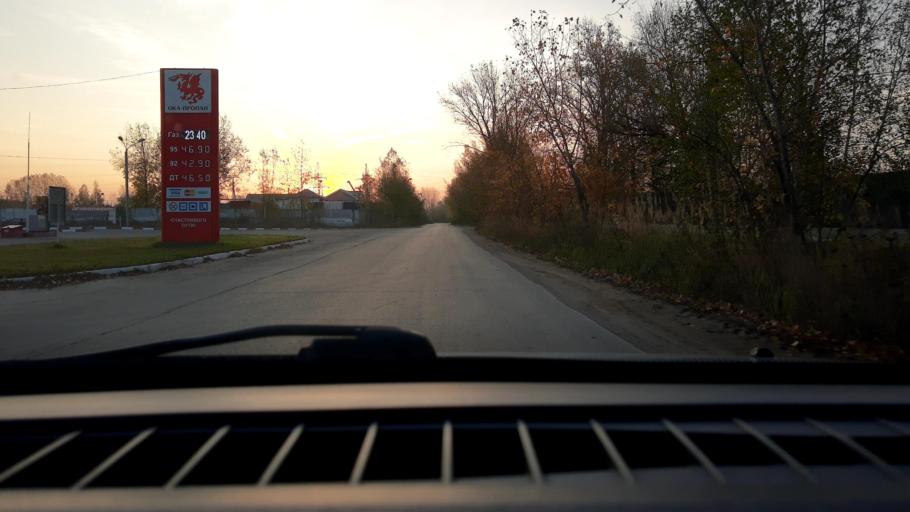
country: RU
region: Nizjnij Novgorod
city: Gorbatovka
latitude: 56.3740
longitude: 43.7920
